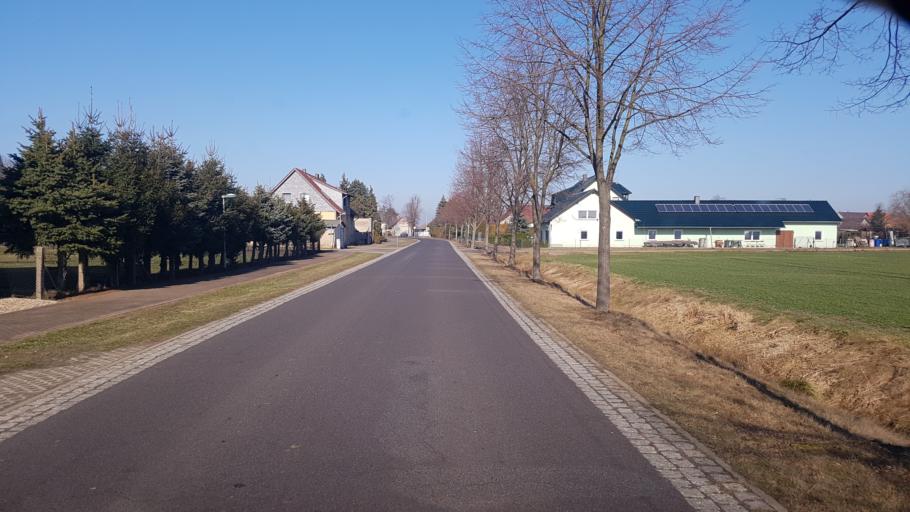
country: DE
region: Brandenburg
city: Ihlow
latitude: 51.8212
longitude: 13.3490
